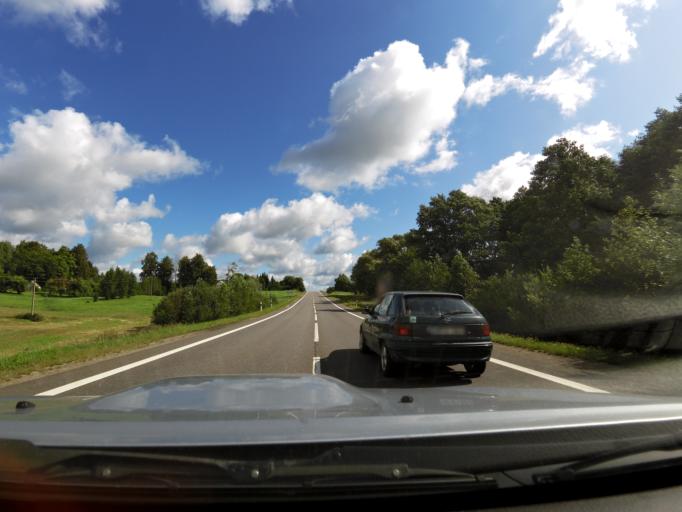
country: LT
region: Utenos apskritis
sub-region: Utena
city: Utena
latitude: 55.5290
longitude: 25.6854
